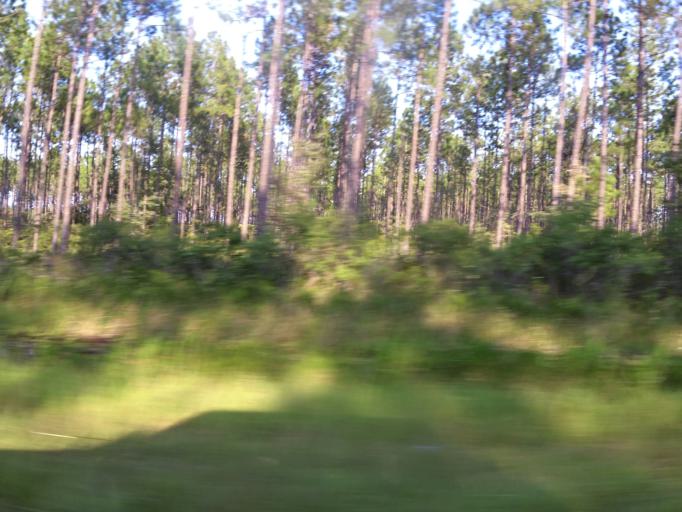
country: US
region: Florida
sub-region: Duval County
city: Baldwin
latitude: 30.3475
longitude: -82.0092
